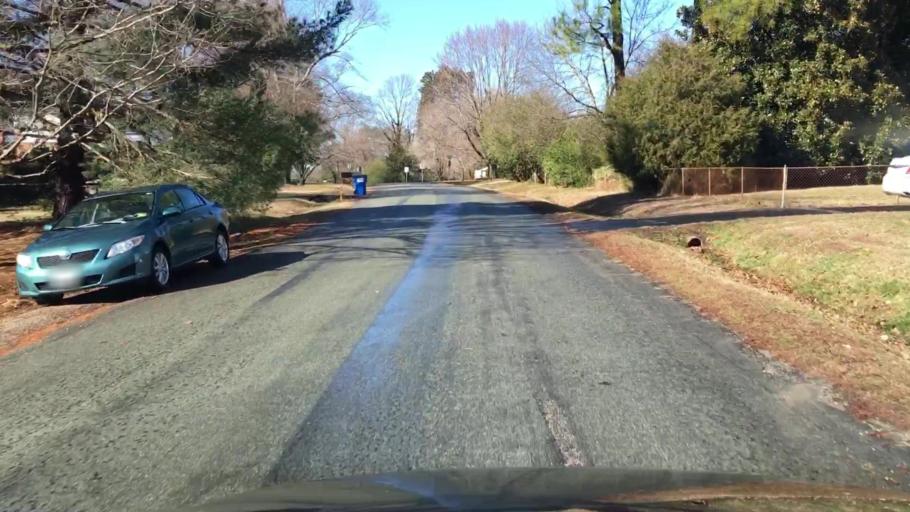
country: US
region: Virginia
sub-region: Chesterfield County
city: Bon Air
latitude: 37.5298
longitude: -77.5911
